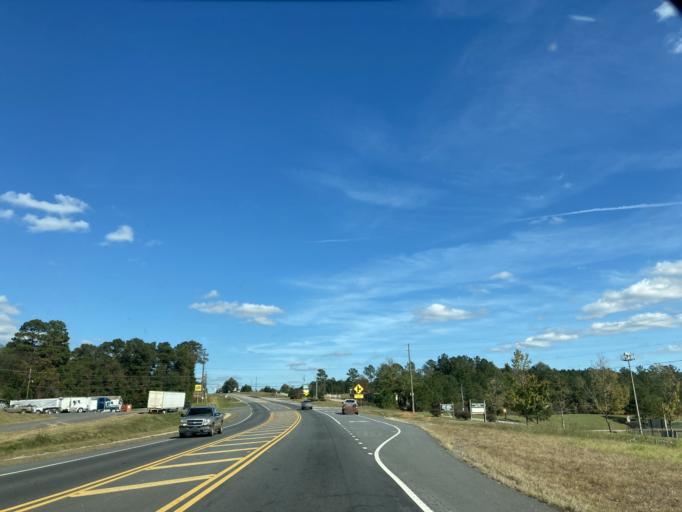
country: US
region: Georgia
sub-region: Bibb County
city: Macon
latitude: 32.8874
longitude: -83.5385
